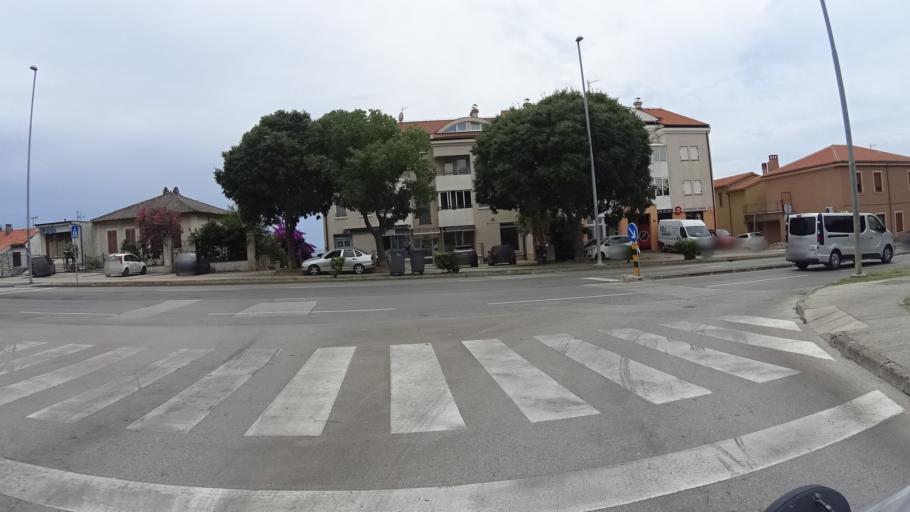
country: HR
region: Istarska
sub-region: Grad Pula
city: Pula
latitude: 44.8535
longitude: 13.8397
